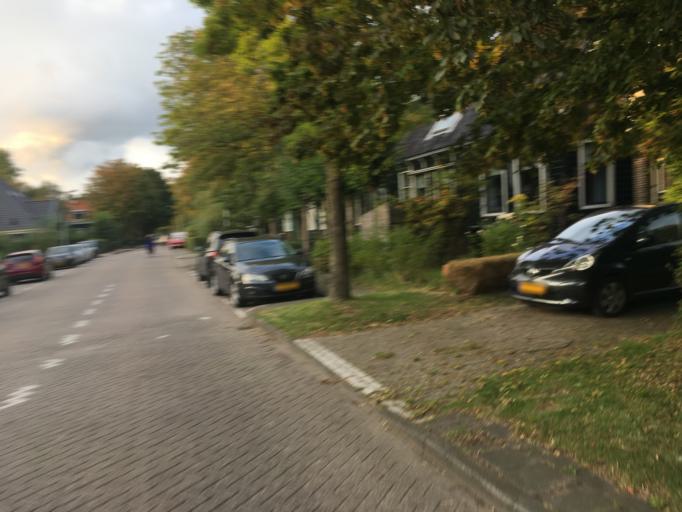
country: NL
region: North Holland
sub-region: Gemeente Zaanstad
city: Zaanstad
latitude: 52.4378
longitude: 4.7791
